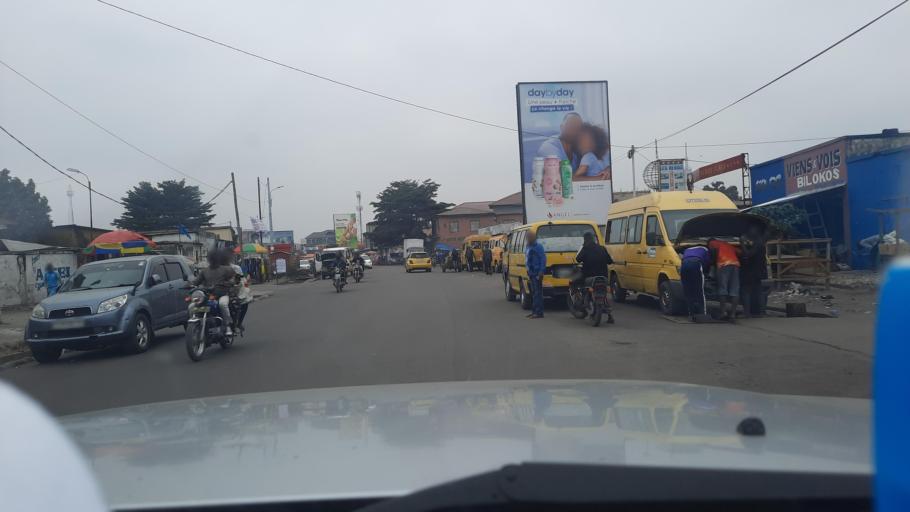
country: CD
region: Kinshasa
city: Masina
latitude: -4.3866
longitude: 15.3448
